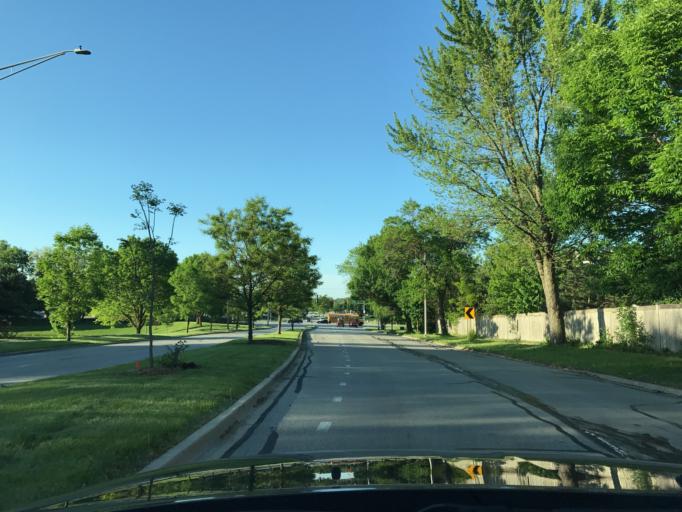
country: US
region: Illinois
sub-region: DuPage County
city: Naperville
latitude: 41.7551
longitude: -88.1156
